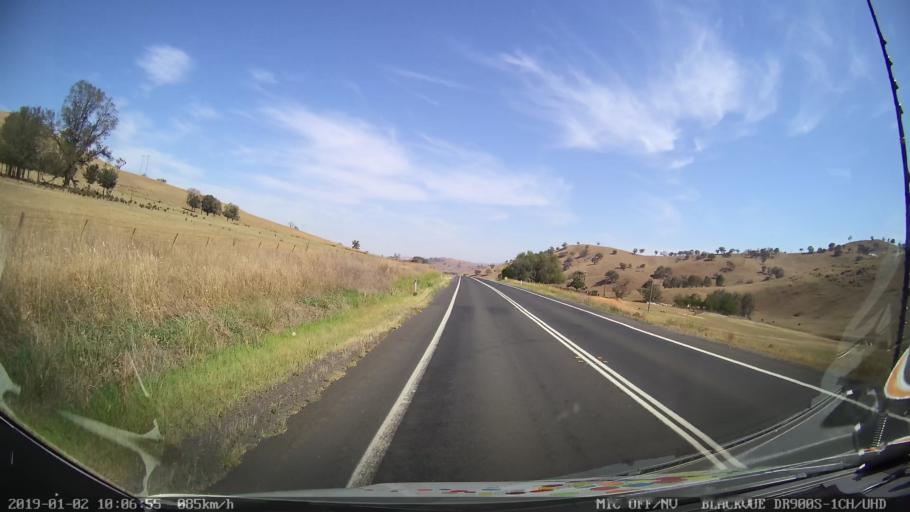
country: AU
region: New South Wales
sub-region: Gundagai
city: Gundagai
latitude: -35.1436
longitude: 148.1177
